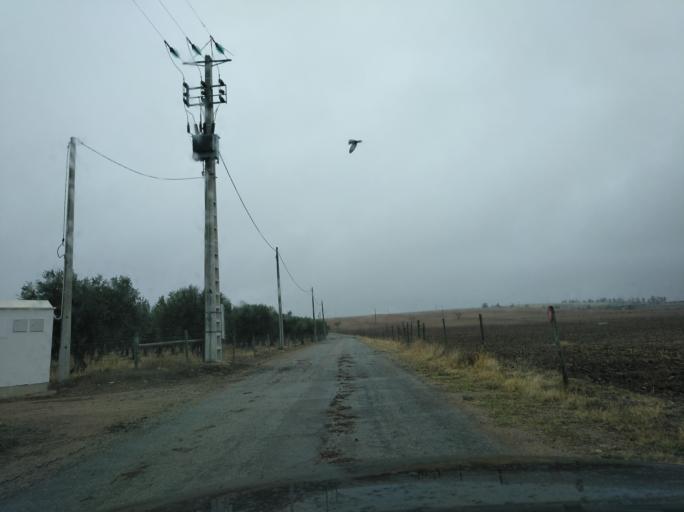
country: PT
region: Portalegre
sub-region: Campo Maior
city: Campo Maior
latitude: 38.9772
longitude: -7.0883
